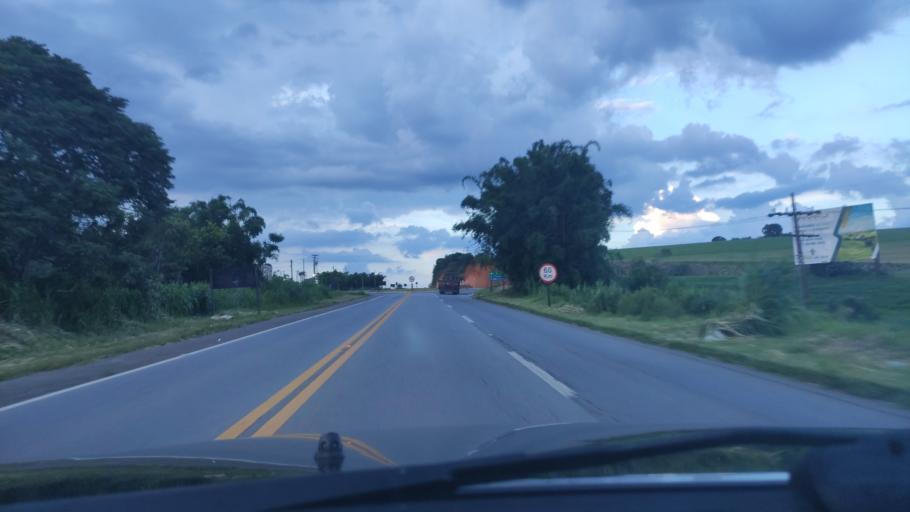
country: BR
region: Sao Paulo
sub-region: Braganca Paulista
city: Braganca Paulista
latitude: -22.8878
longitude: -46.5399
